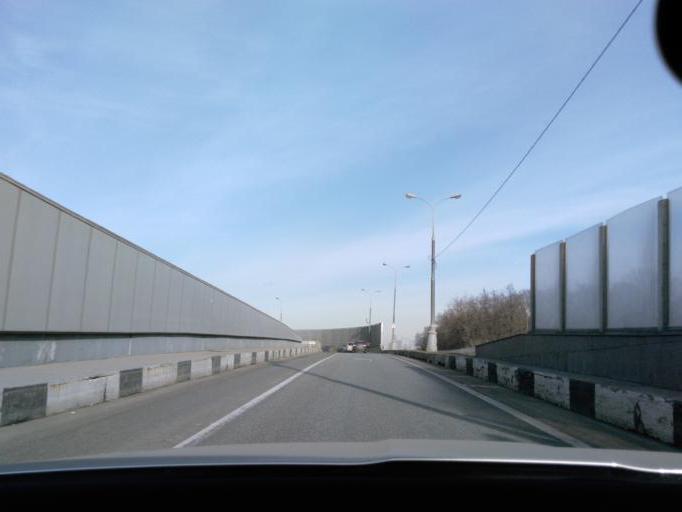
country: RU
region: Moscow
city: Novyye Cheremushki
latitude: 55.7107
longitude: 37.5821
